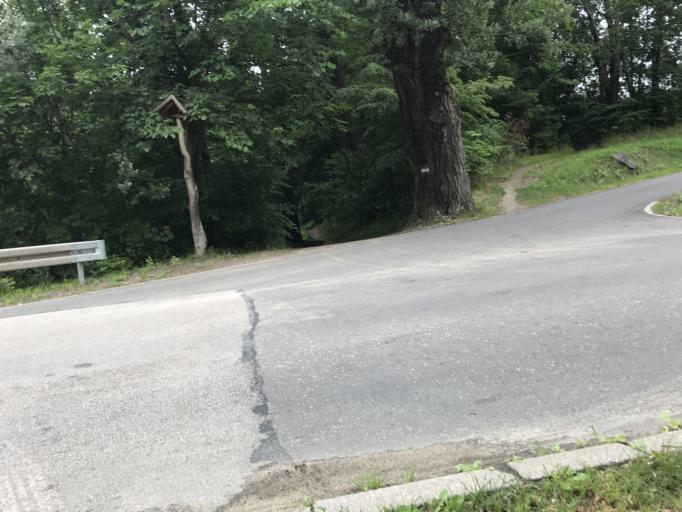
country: PL
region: Warmian-Masurian Voivodeship
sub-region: Powiat elblaski
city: Elblag
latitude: 54.1754
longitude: 19.4361
